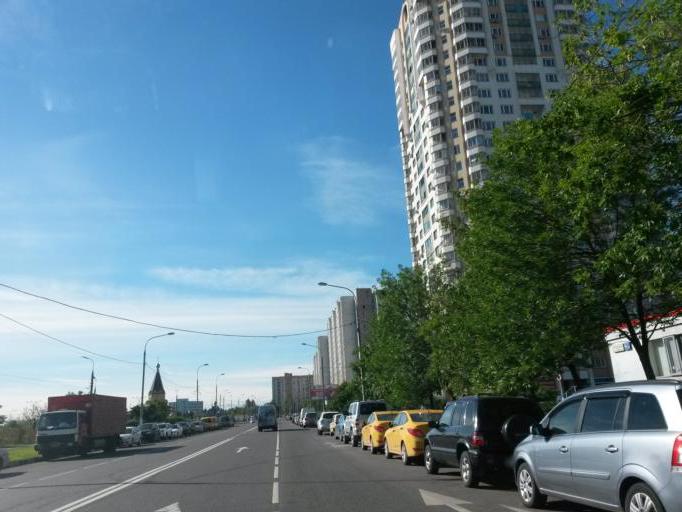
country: RU
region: Moscow
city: Brateyevo
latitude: 55.6349
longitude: 37.7610
